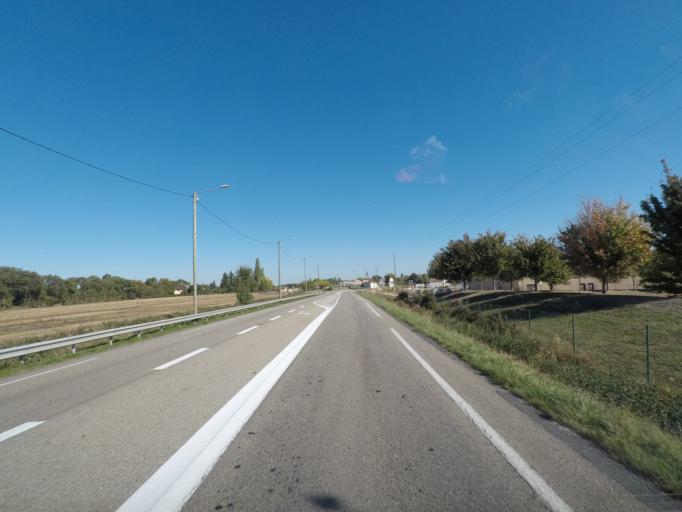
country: FR
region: Rhone-Alpes
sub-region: Departement de l'Ain
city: Servas
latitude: 46.1276
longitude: 5.1609
